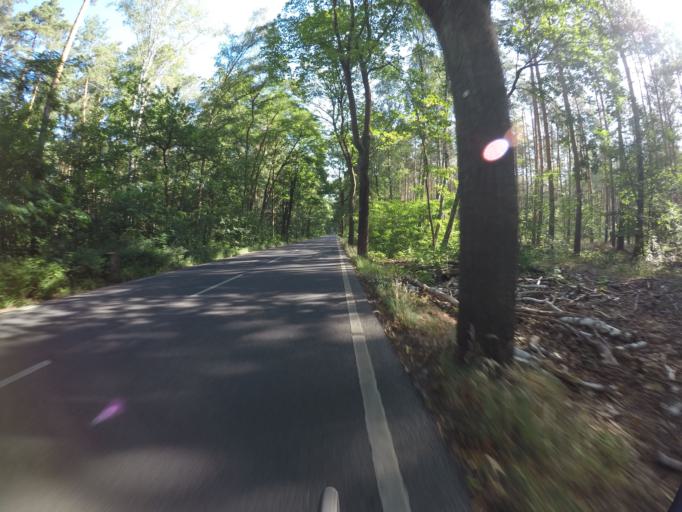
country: DE
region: Berlin
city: Schmockwitz
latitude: 52.3594
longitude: 13.6514
